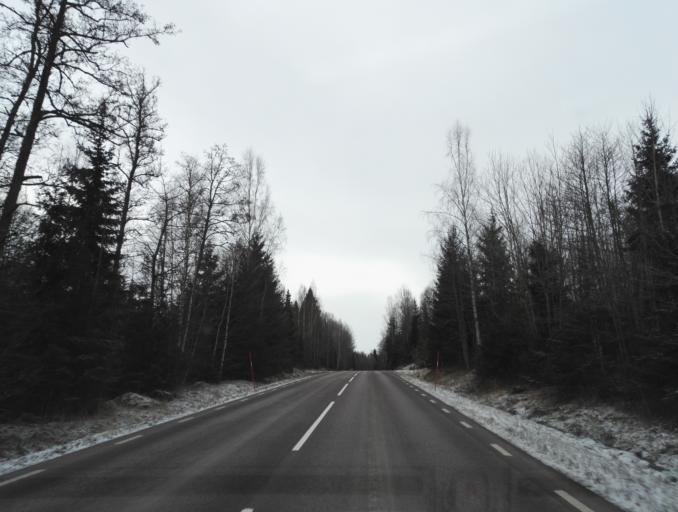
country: SE
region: Kalmar
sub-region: Hultsfreds Kommun
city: Virserum
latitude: 57.3754
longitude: 15.6066
